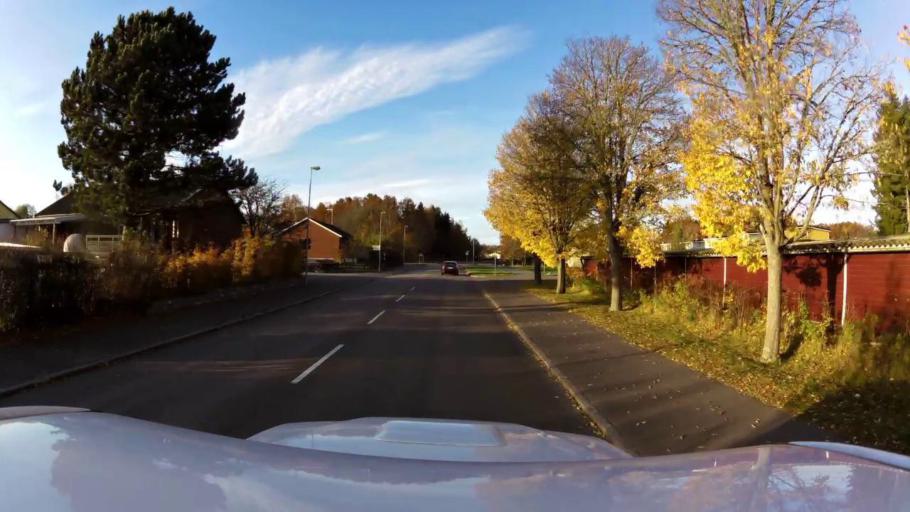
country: SE
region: OEstergoetland
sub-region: Linkopings Kommun
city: Sturefors
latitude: 58.3352
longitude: 15.7219
